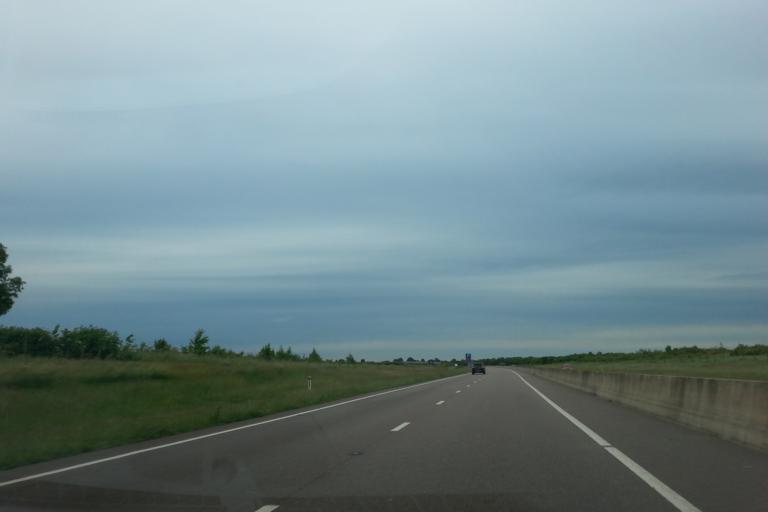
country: GB
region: England
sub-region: Nottinghamshire
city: East Bridgford
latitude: 52.9794
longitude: -0.9471
